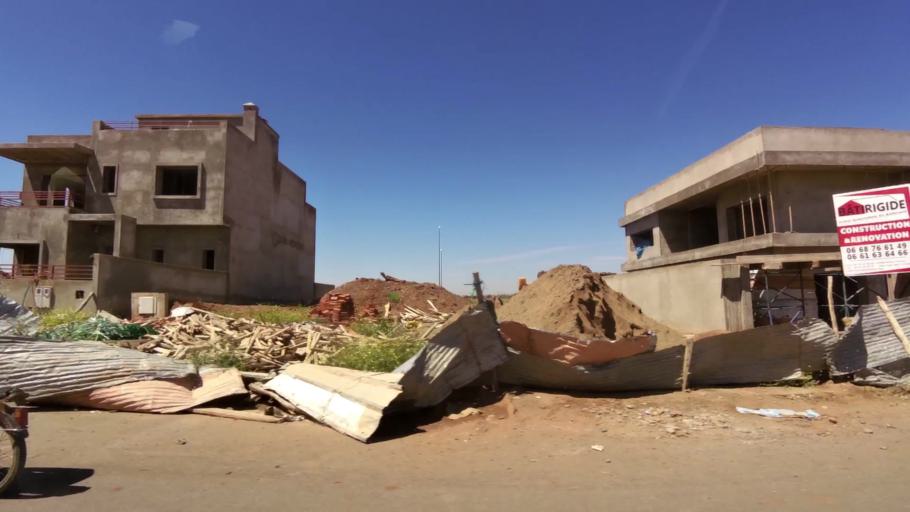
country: MA
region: Marrakech-Tensift-Al Haouz
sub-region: Marrakech
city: Marrakesh
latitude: 31.5783
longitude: -7.9877
